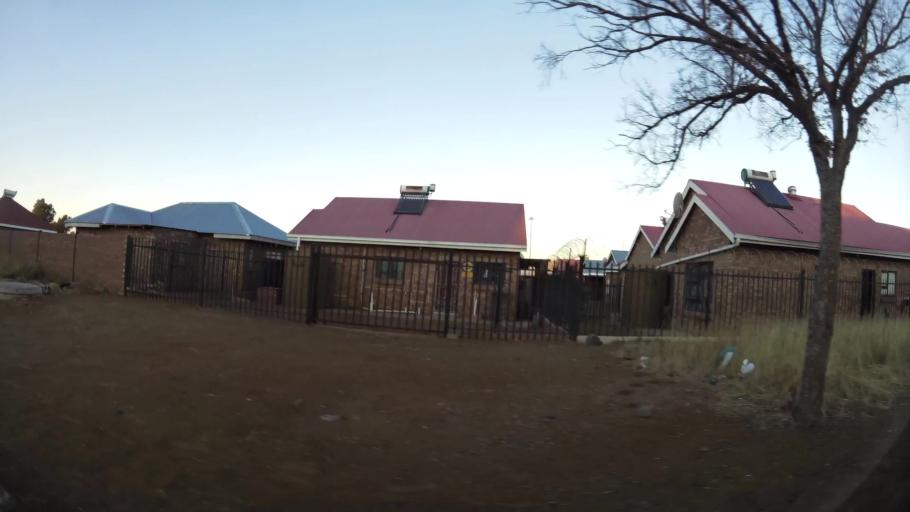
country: ZA
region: Northern Cape
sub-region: Frances Baard District Municipality
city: Kimberley
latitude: -28.7316
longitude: 24.7760
